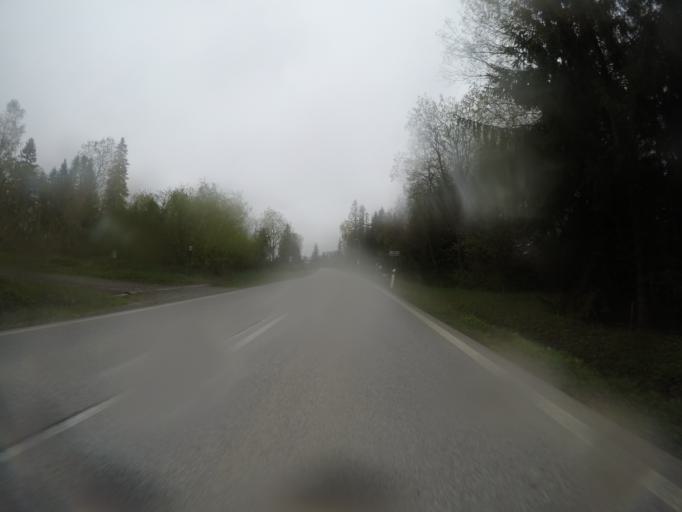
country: SK
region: Presovsky
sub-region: Okres Poprad
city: Strba
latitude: 49.0940
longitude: 20.0688
